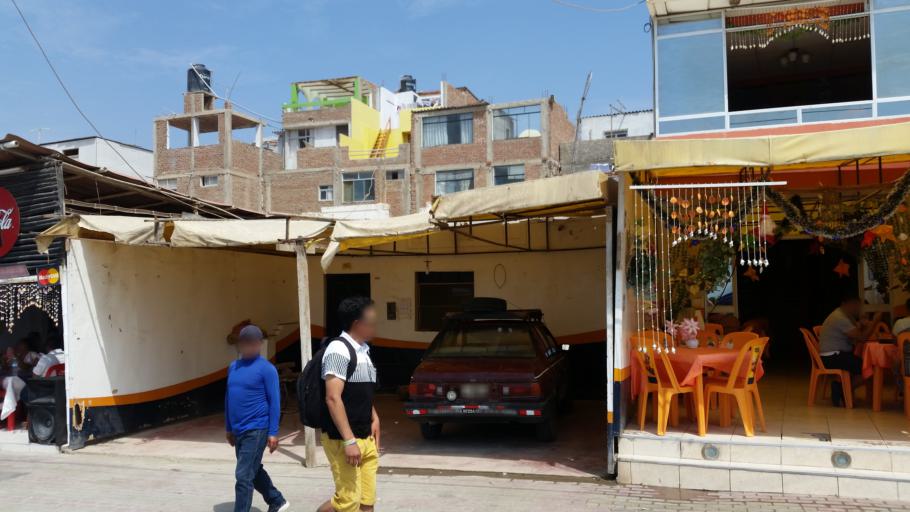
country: PE
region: Lambayeque
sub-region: Provincia de Chiclayo
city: Pimentel
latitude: -6.8421
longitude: -79.9375
